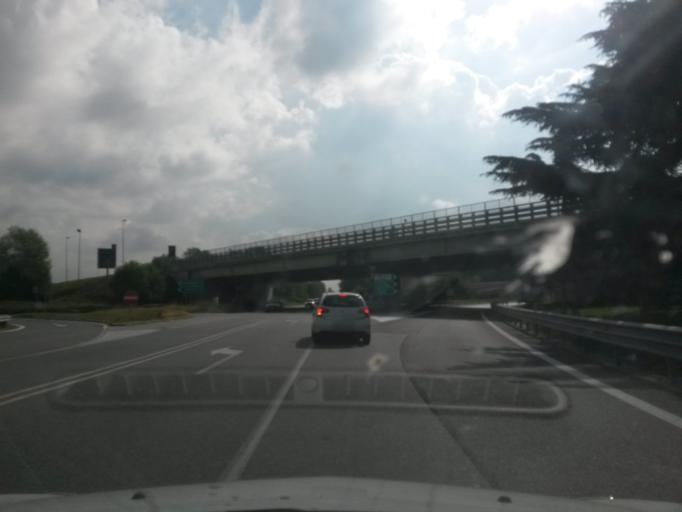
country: IT
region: Piedmont
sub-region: Provincia di Torino
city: Alpignano
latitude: 45.0820
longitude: 7.5031
